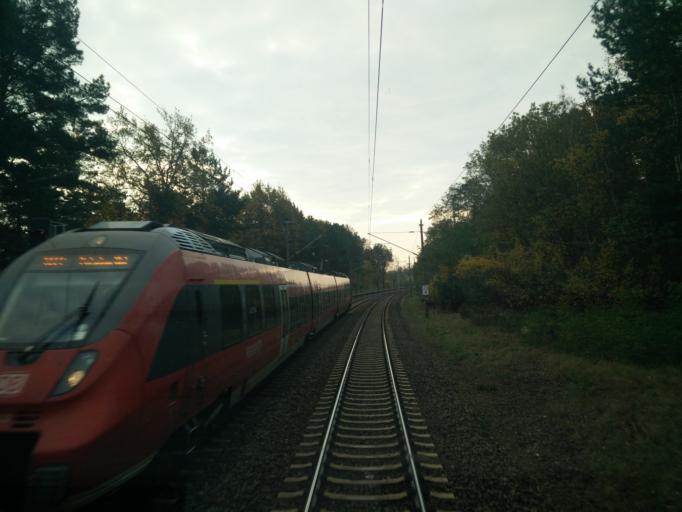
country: DE
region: Brandenburg
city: Wildau
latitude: 52.3350
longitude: 13.6362
